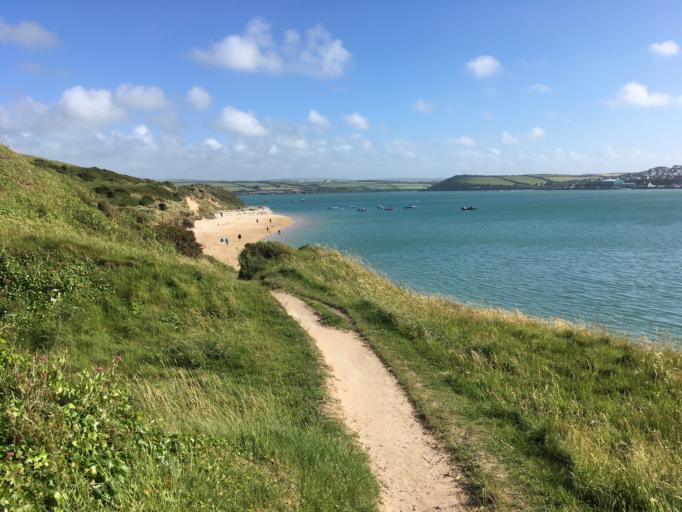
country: GB
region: England
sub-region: Cornwall
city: Padstow
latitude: 50.5491
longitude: -4.9263
